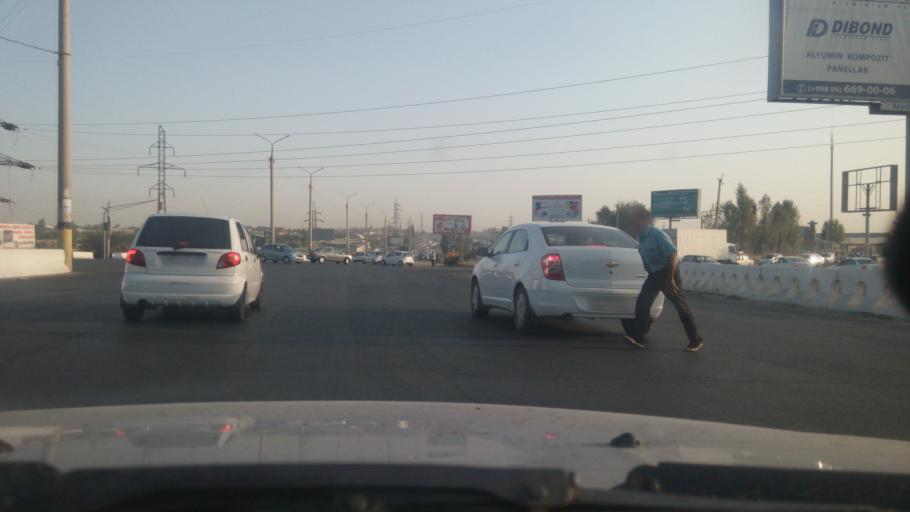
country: UZ
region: Toshkent Shahri
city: Tashkent
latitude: 41.2771
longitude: 69.1467
